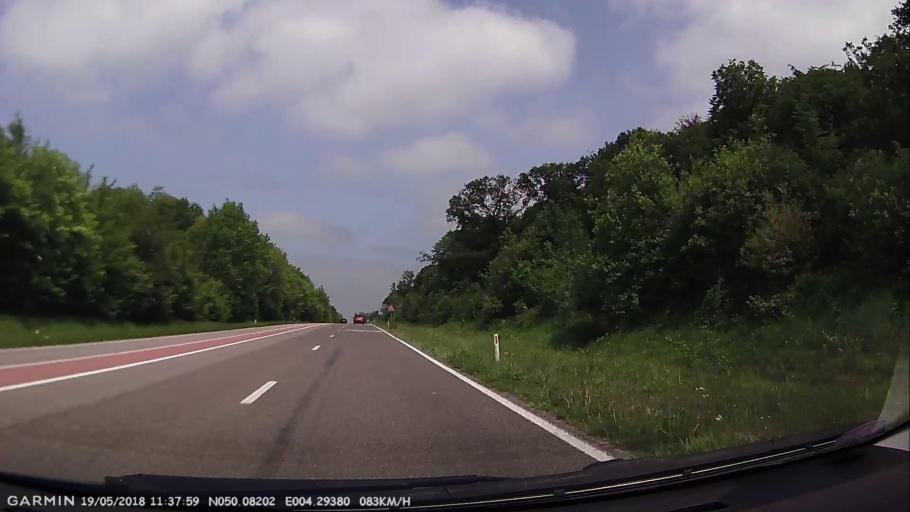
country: BE
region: Wallonia
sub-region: Province du Hainaut
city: Chimay
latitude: 50.0823
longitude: 4.2938
